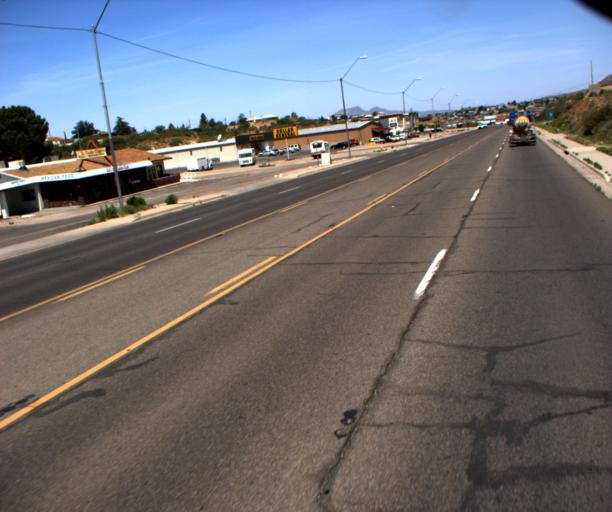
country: US
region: Arizona
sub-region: Gila County
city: Globe
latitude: 33.3856
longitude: -110.7581
